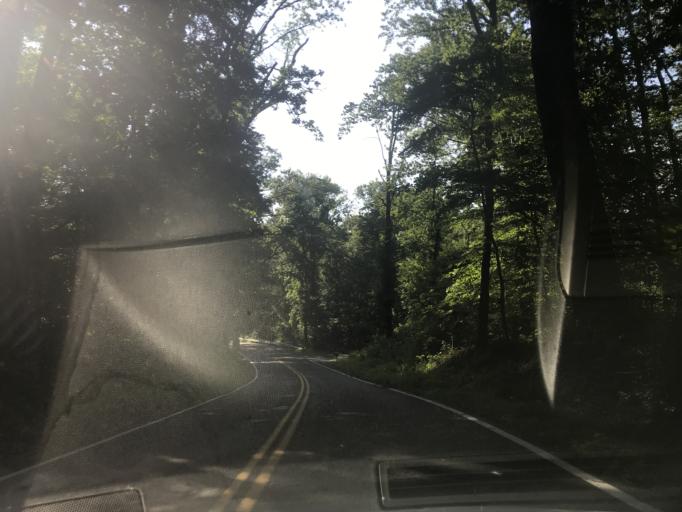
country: US
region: Maryland
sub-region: Harford County
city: Aberdeen
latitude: 39.5184
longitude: -76.1247
